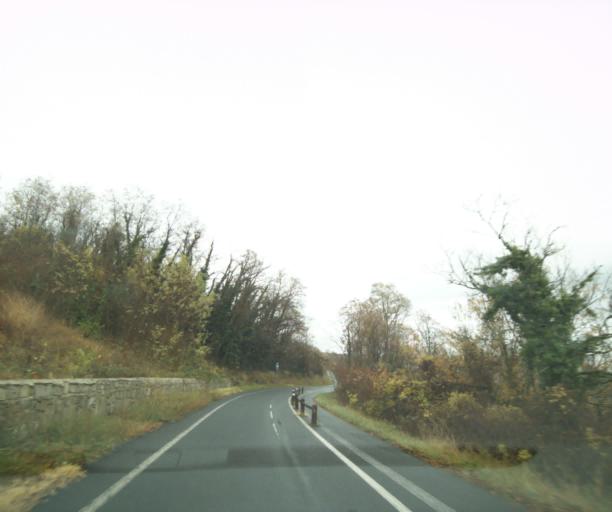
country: FR
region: Auvergne
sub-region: Departement du Puy-de-Dome
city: Cournon-d'Auvergne
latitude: 45.7521
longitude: 3.2055
